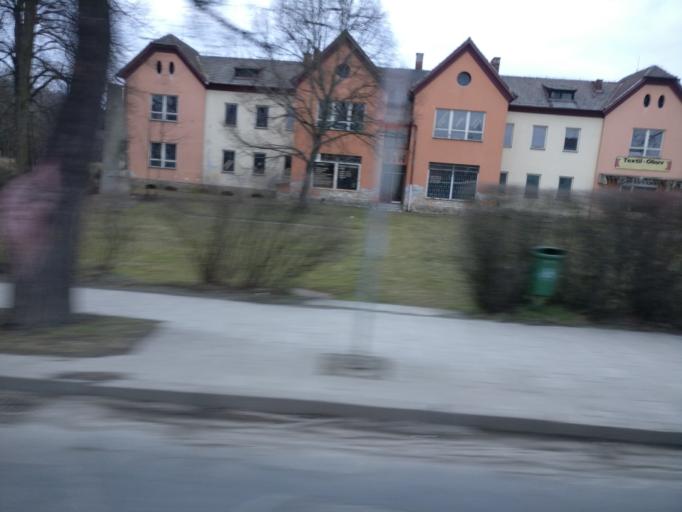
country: CZ
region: South Moravian
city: Zastavka
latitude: 49.1877
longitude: 16.3622
